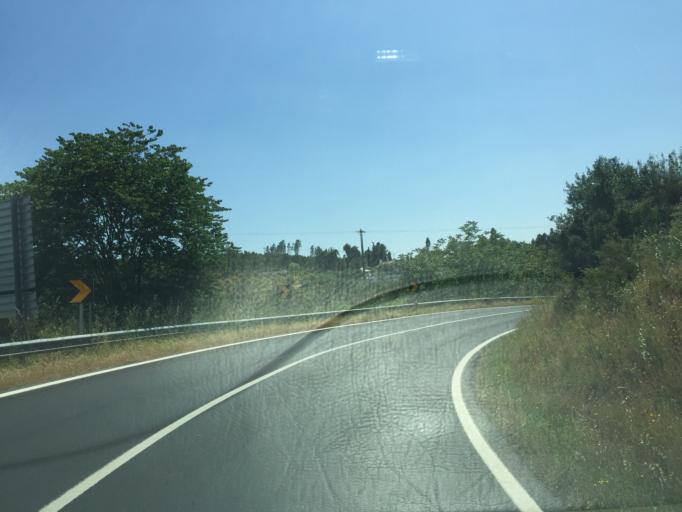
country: PT
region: Santarem
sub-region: Constancia
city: Constancia
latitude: 39.4760
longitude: -8.3443
